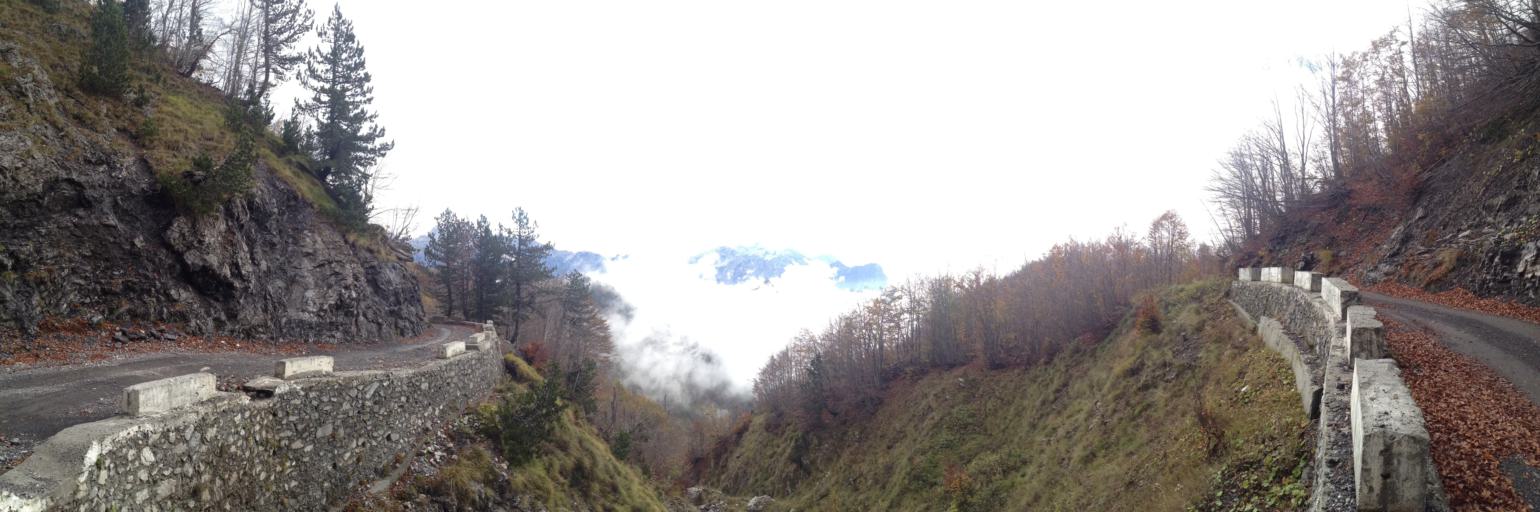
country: AL
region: Shkoder
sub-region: Rrethi i Shkodres
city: Nicaj-Shale
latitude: 42.3877
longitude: 19.7363
